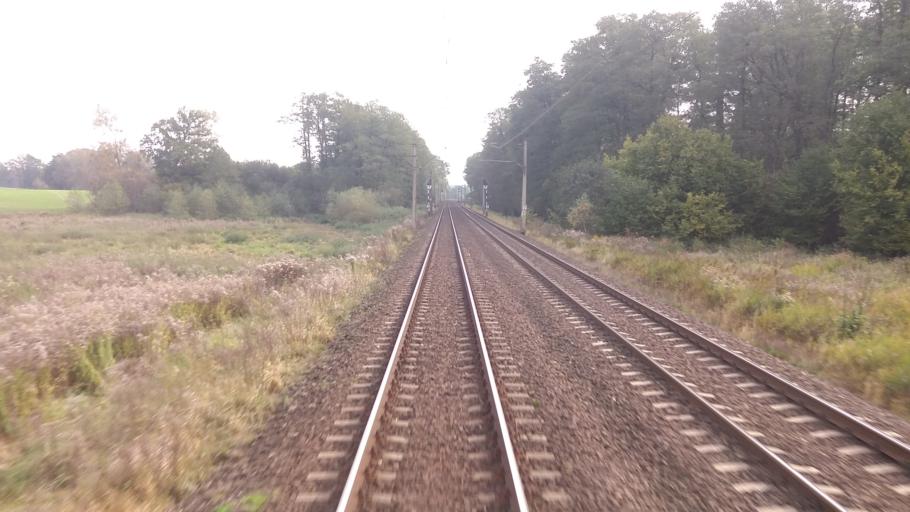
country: PL
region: West Pomeranian Voivodeship
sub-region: Powiat stargardzki
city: Dolice
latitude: 53.1841
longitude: 15.2649
